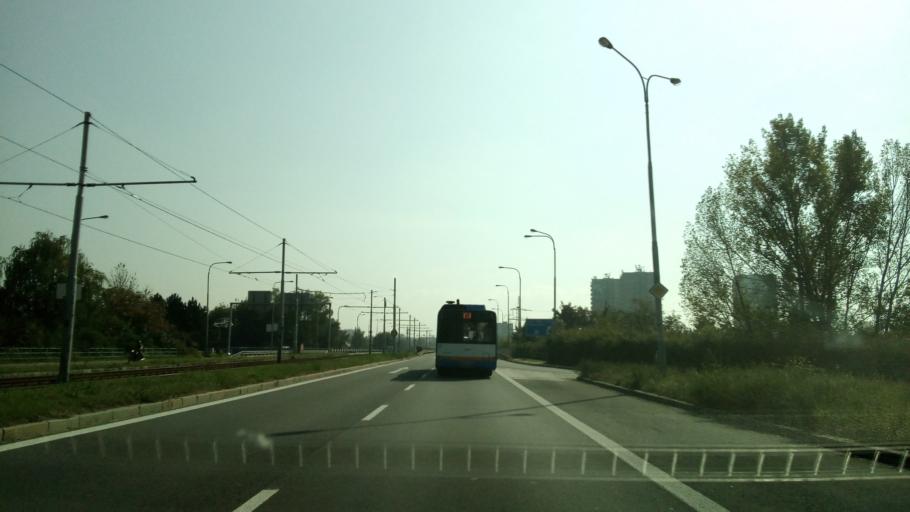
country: CZ
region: Moravskoslezsky
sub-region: Okres Ostrava-Mesto
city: Ostrava
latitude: 49.7997
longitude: 18.2471
